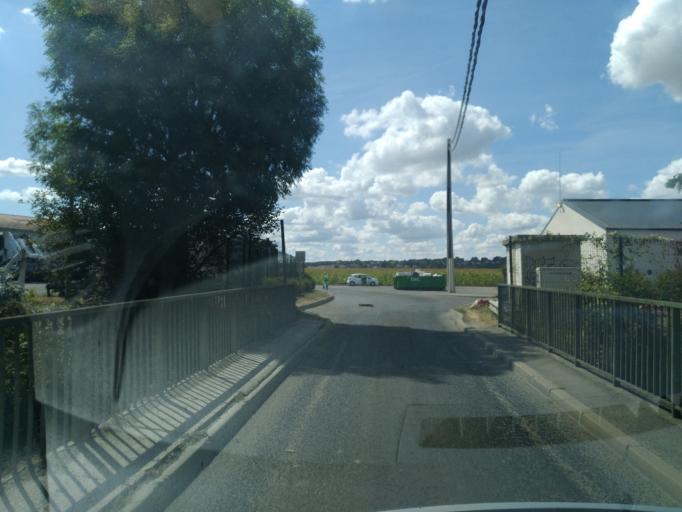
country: FR
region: Ile-de-France
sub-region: Departement des Yvelines
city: Thiverval-Grignon
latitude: 48.8331
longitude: 1.9289
